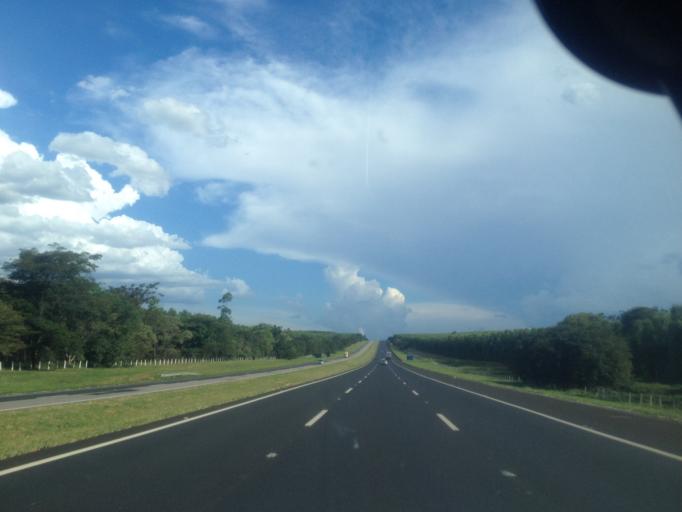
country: BR
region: Sao Paulo
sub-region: Sao Simao
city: Sao Simao
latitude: -21.5907
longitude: -47.6244
